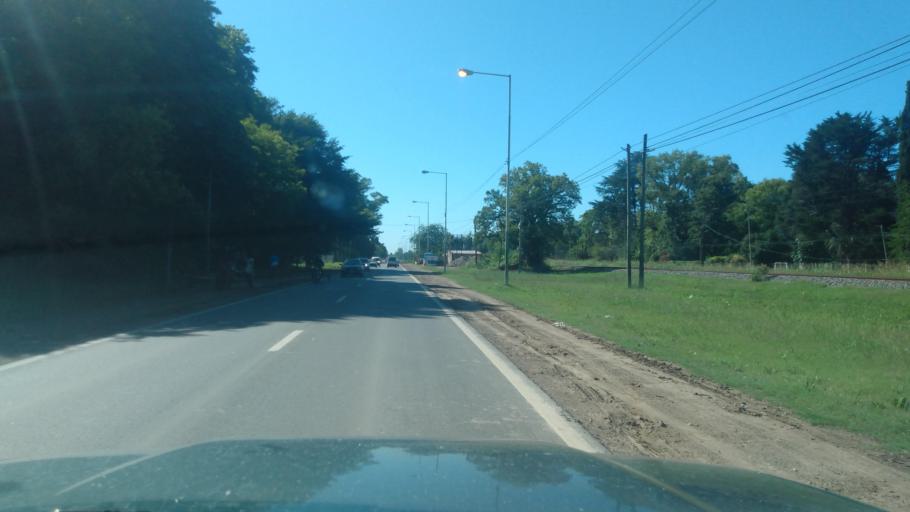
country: AR
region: Buenos Aires
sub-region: Partido de General Rodriguez
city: General Rodriguez
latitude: -34.6030
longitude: -58.9769
